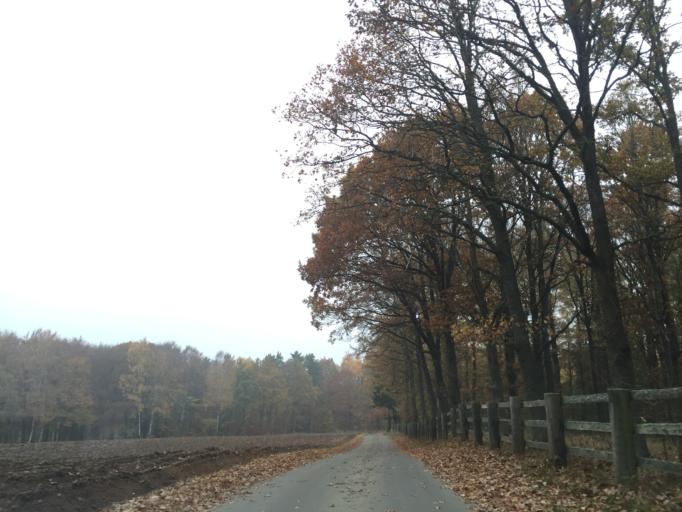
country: SE
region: Skane
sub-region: Lunds Kommun
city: Veberod
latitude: 55.6137
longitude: 13.5100
